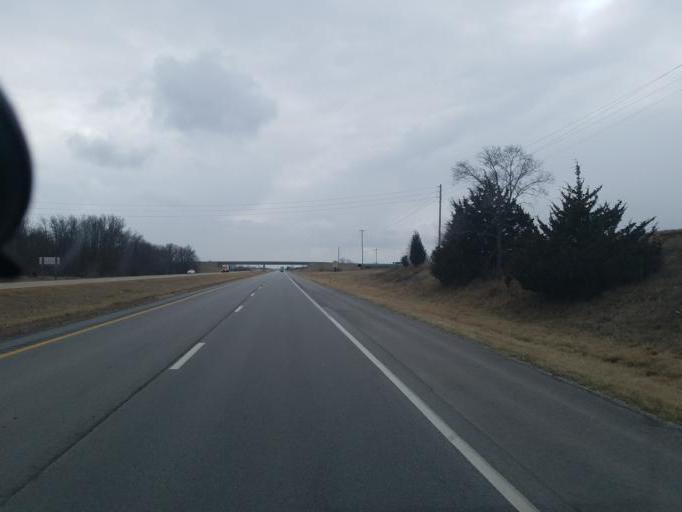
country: US
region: Missouri
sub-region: Randolph County
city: Moberly
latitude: 39.4125
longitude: -92.4124
